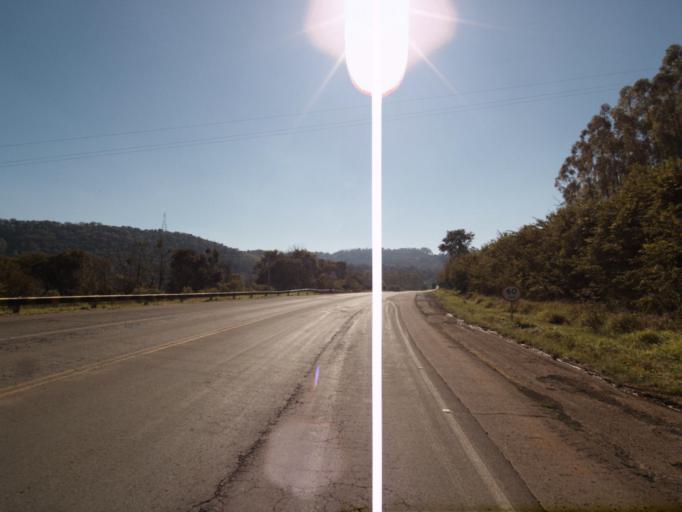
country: BR
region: Rio Grande do Sul
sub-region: Frederico Westphalen
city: Frederico Westphalen
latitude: -27.0726
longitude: -53.2313
